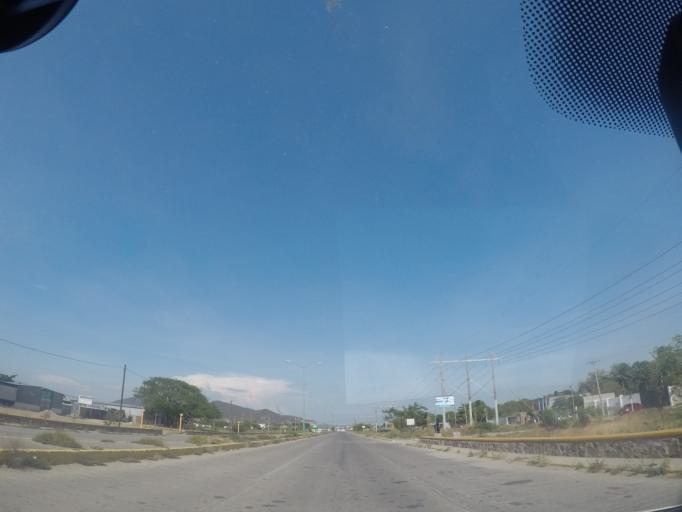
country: MX
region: Oaxaca
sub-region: Salina Cruz
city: Salina Cruz
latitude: 16.2204
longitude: -95.1970
